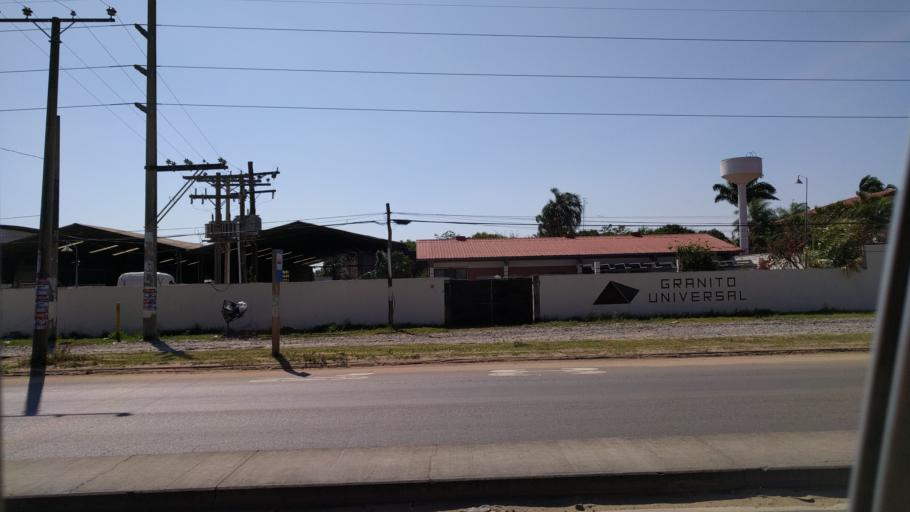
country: BO
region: Santa Cruz
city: Cotoca
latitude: -17.7657
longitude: -63.1063
